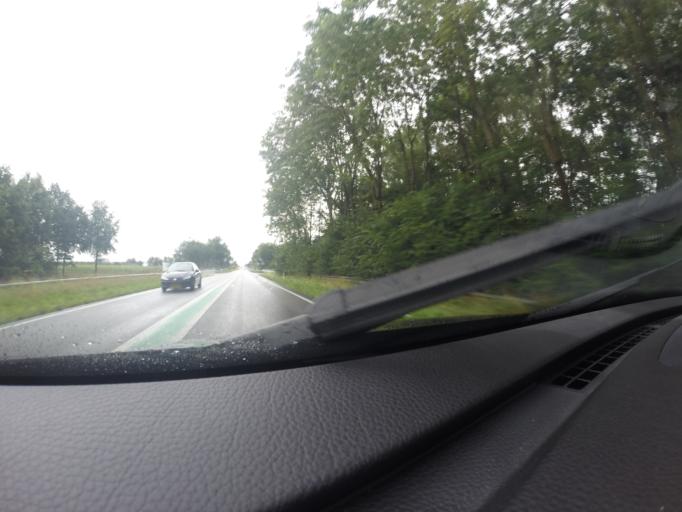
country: NL
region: Gelderland
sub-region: Gemeente Lochem
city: Laren
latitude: 52.2425
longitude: 6.3989
